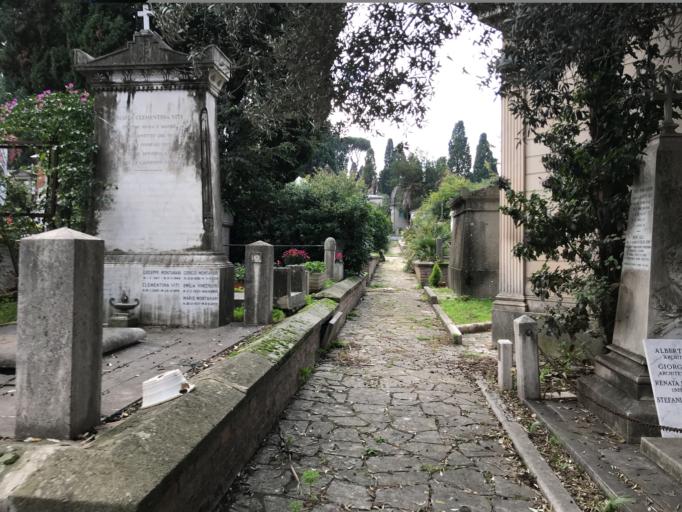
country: IT
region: Latium
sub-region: Citta metropolitana di Roma Capitale
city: Rome
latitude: 41.9047
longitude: 12.5224
